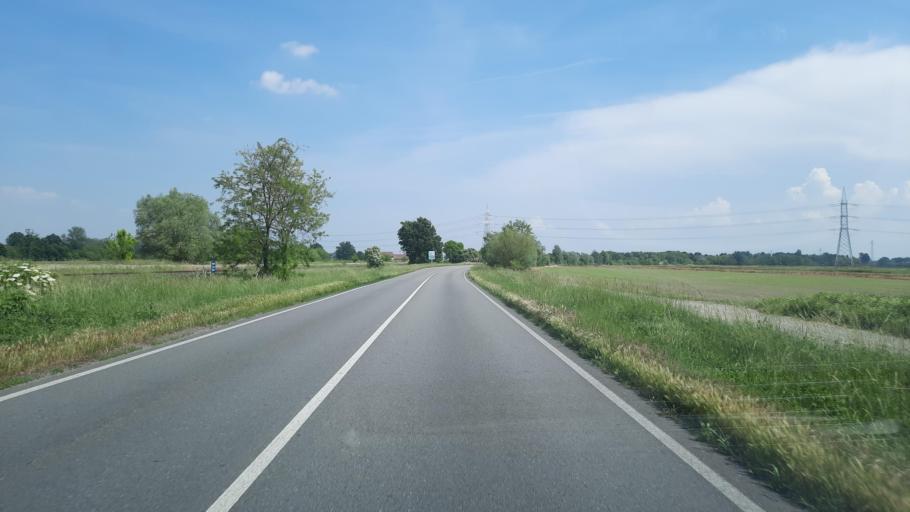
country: IT
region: Lombardy
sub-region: Provincia di Pavia
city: Dorno
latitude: 45.1868
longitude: 8.9563
